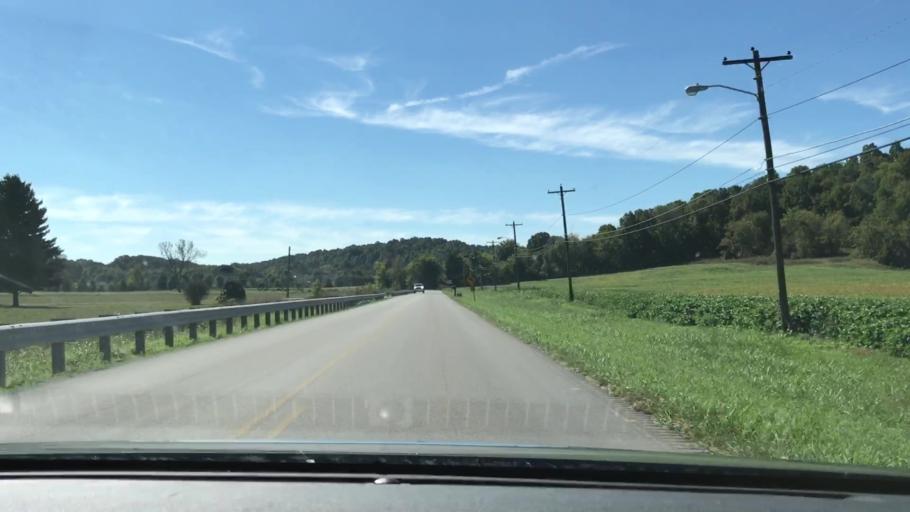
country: US
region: Kentucky
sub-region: Logan County
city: Russellville
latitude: 36.8393
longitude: -86.8705
